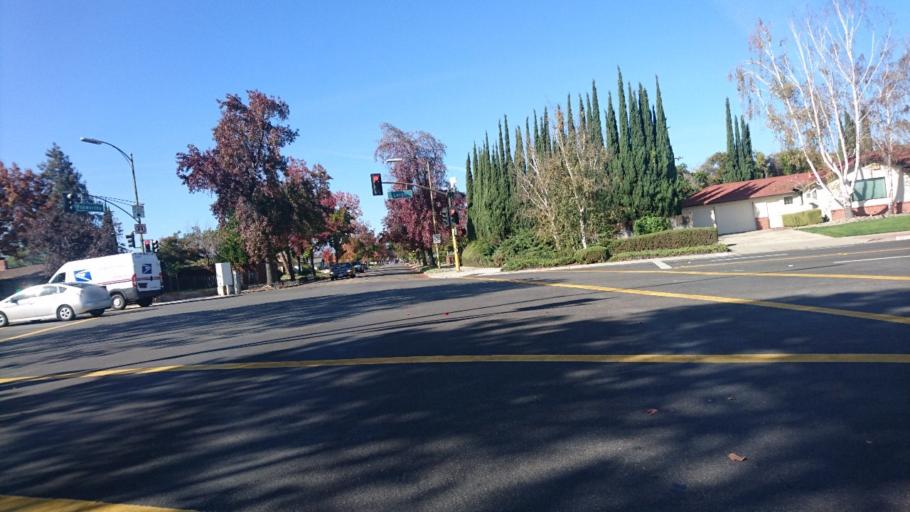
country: US
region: California
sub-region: Santa Clara County
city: Cambrian Park
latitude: 37.2674
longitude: -121.9221
